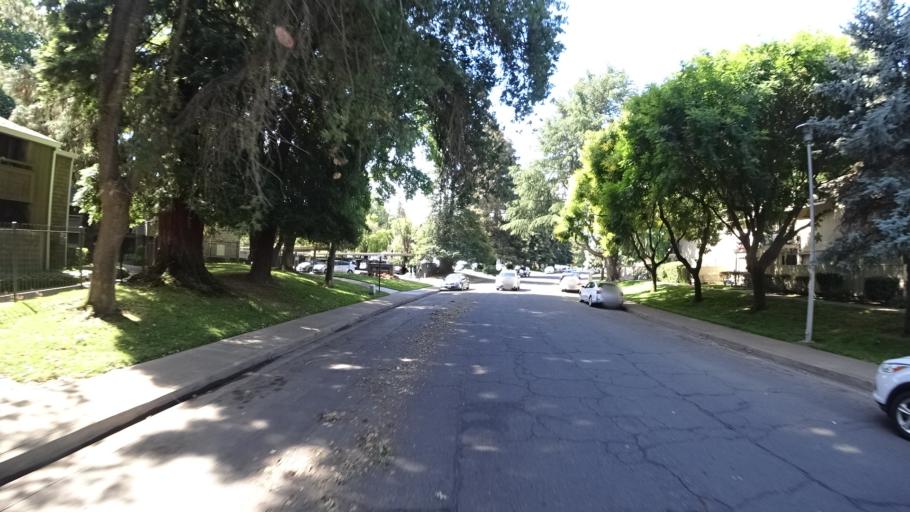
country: US
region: California
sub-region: Sacramento County
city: Arden-Arcade
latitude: 38.5737
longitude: -121.4186
